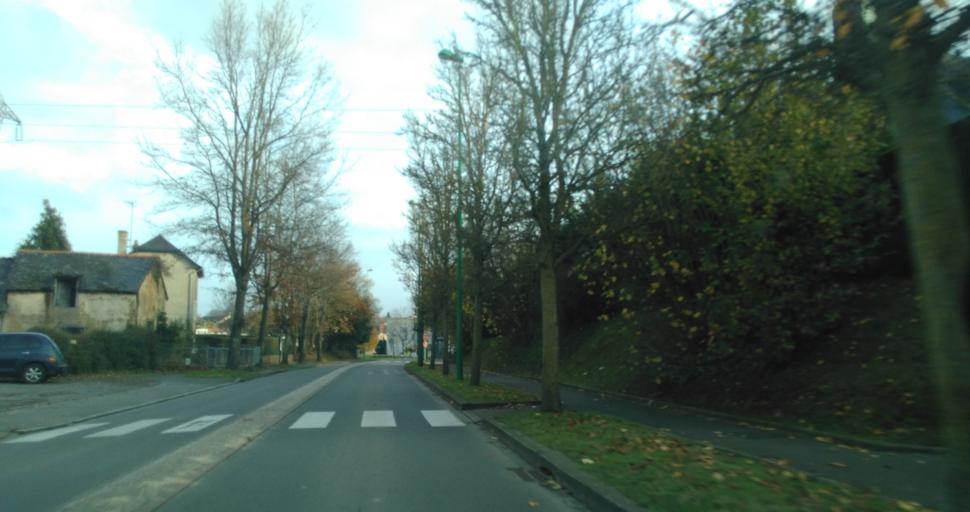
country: FR
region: Brittany
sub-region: Departement d'Ille-et-Vilaine
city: Vezin-le-Coquet
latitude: 48.1195
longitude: -1.7622
